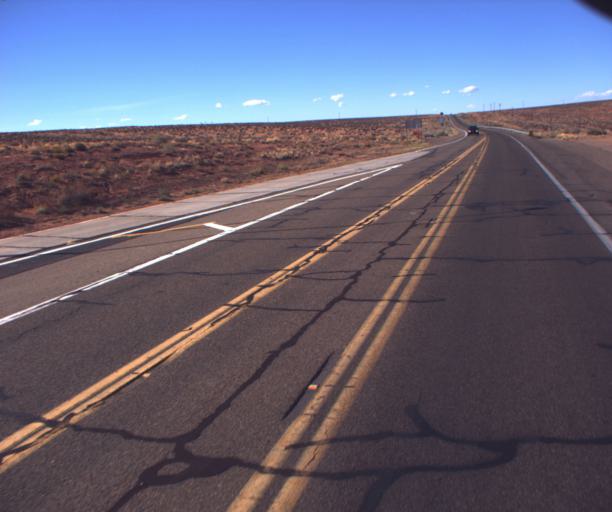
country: US
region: Arizona
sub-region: Coconino County
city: Page
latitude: 36.9522
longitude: -111.4989
